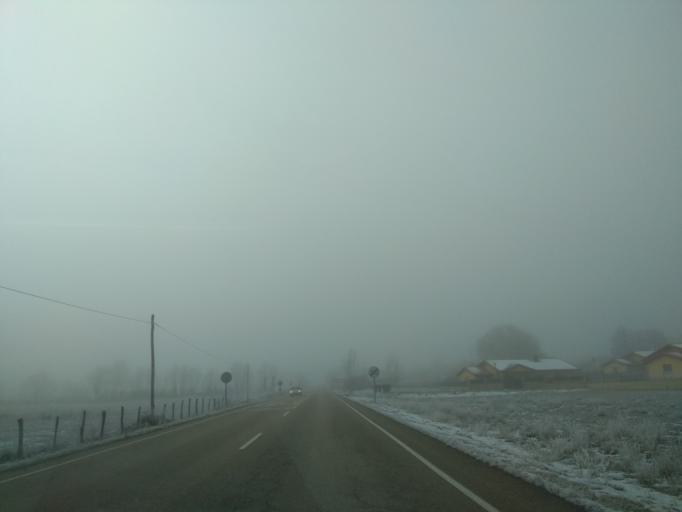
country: ES
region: Castille and Leon
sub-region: Provincia de Burgos
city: Espinosa de los Monteros
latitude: 43.0393
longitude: -3.4939
